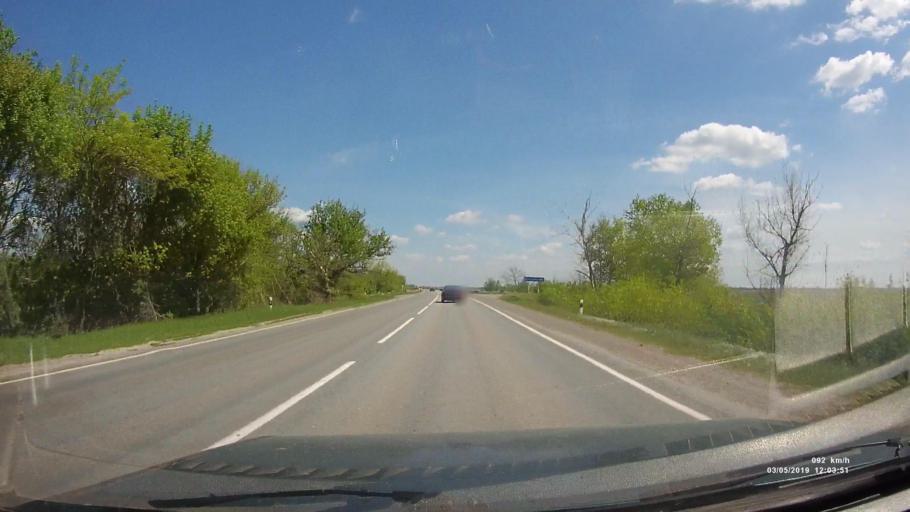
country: RU
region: Rostov
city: Bagayevskaya
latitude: 47.2747
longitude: 40.3989
